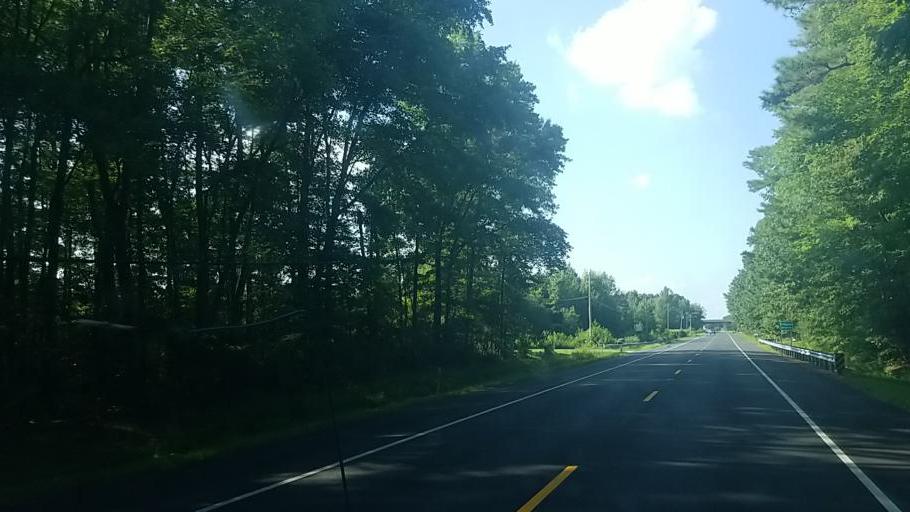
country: US
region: Maryland
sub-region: Worcester County
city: Ocean Pines
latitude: 38.3735
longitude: -75.1985
